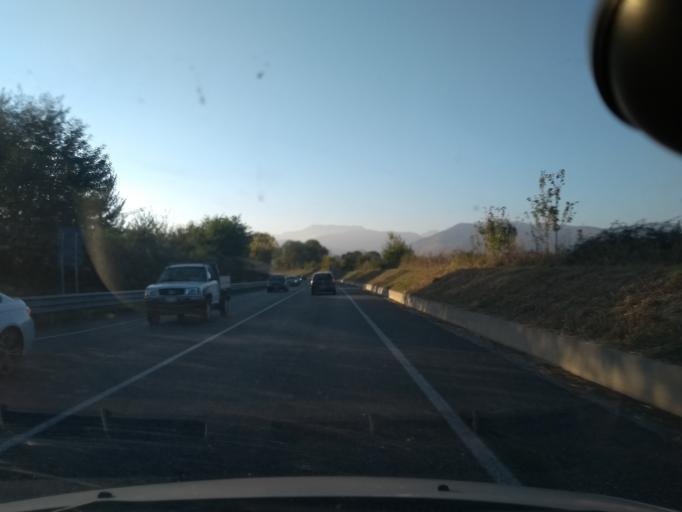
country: IT
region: Piedmont
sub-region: Provincia di Torino
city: Pianezza
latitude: 45.1168
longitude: 7.5505
